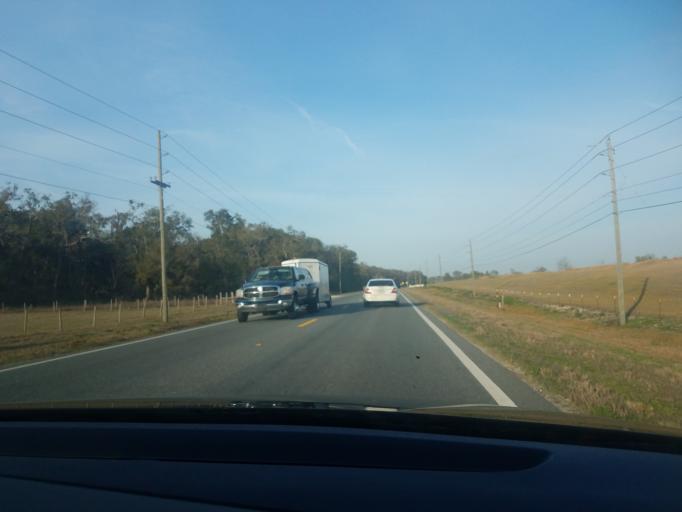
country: US
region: Florida
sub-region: Sumter County
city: Lake Panasoffkee
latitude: 28.7559
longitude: -82.0442
